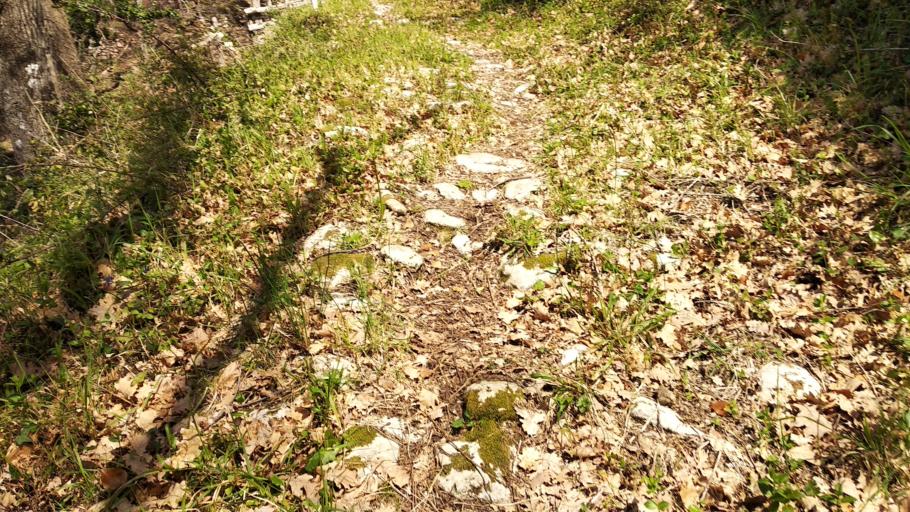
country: IT
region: Calabria
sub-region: Provincia di Cosenza
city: Altilia
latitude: 39.1285
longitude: 16.2494
